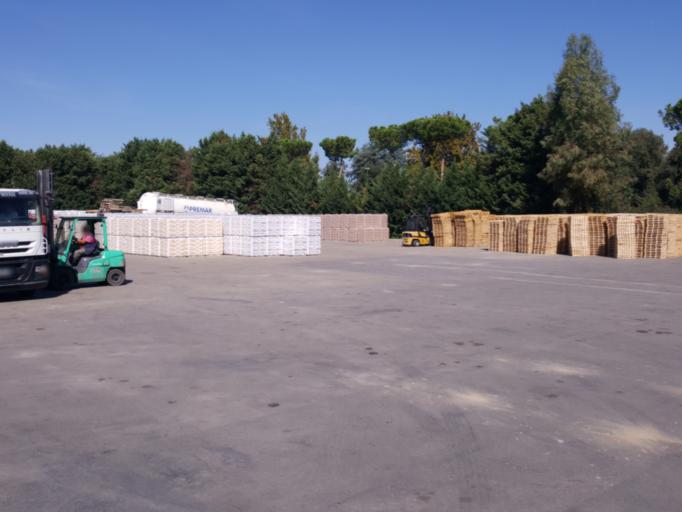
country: IT
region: Campania
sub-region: Provincia di Napoli
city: Caivano
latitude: 40.9655
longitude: 14.3020
